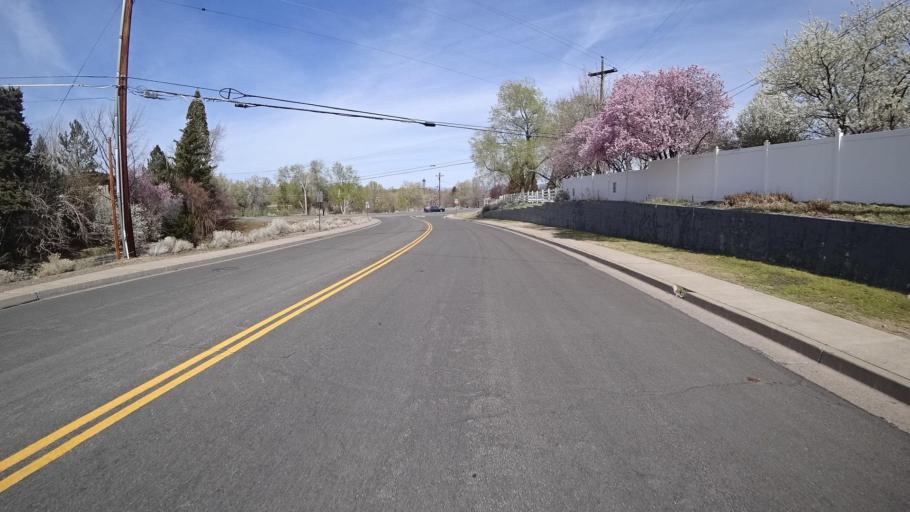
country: US
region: Nevada
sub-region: Washoe County
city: Reno
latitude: 39.4910
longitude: -119.8218
